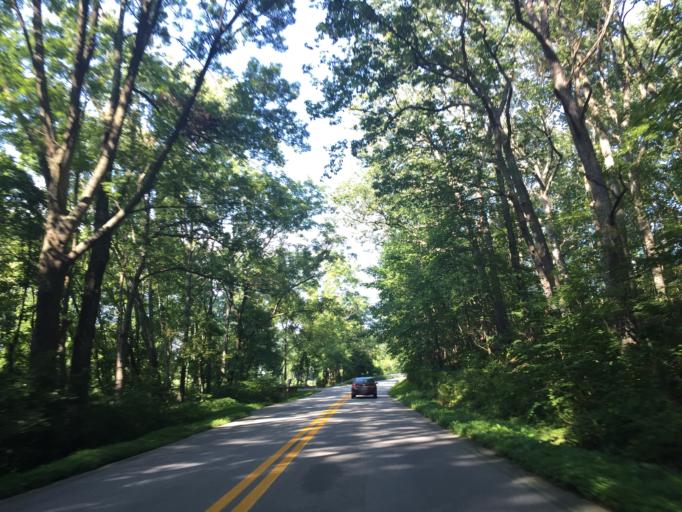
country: US
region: Maryland
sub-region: Carroll County
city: Manchester
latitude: 39.6306
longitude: -76.8891
